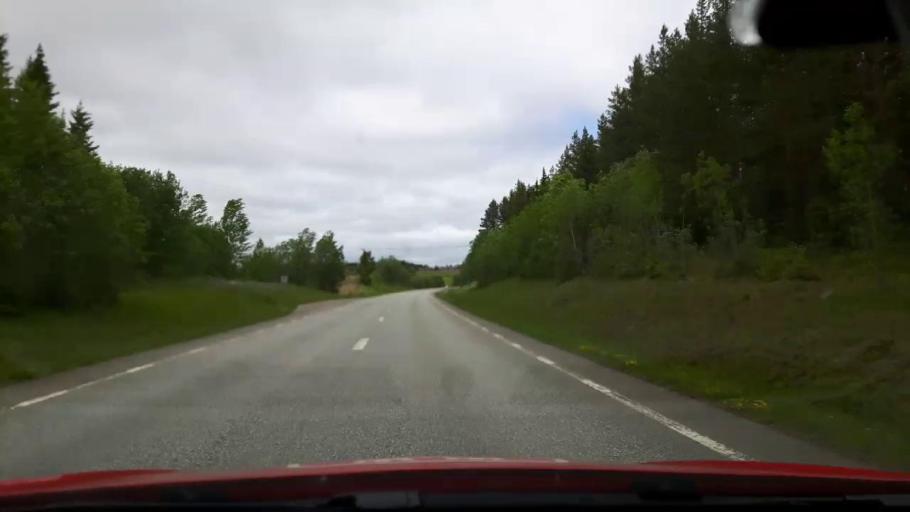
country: SE
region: Jaemtland
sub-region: Krokoms Kommun
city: Krokom
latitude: 63.5112
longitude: 14.5204
